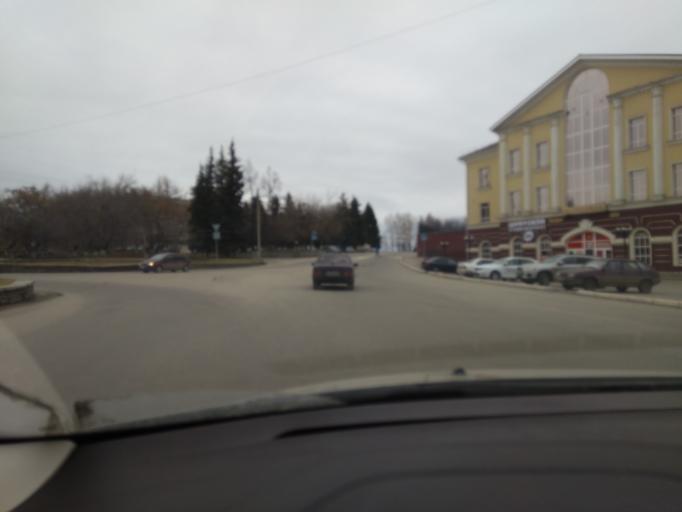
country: RU
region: Chelyabinsk
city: Kyshtym
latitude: 55.7080
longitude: 60.5386
